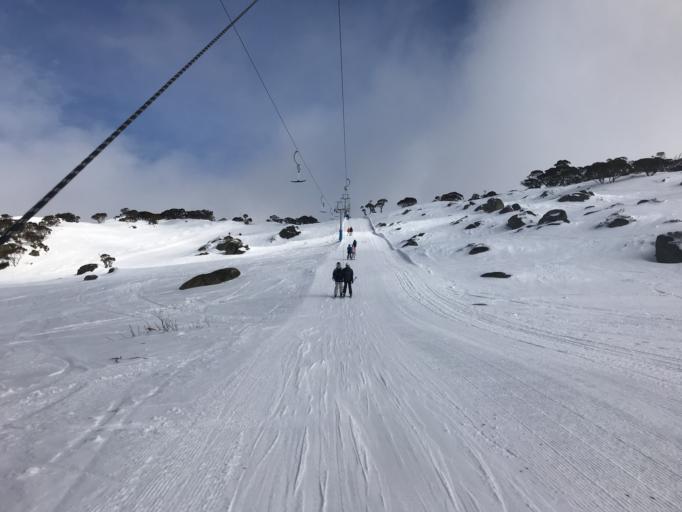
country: AU
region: New South Wales
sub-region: Snowy River
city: Jindabyne
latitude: -36.3864
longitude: 148.3974
